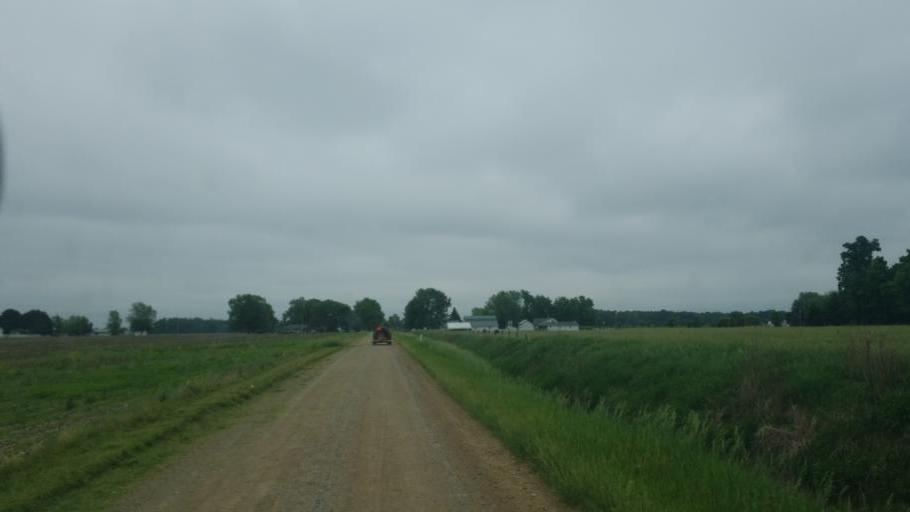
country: US
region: Indiana
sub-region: Elkhart County
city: Nappanee
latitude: 41.4605
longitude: -86.0400
